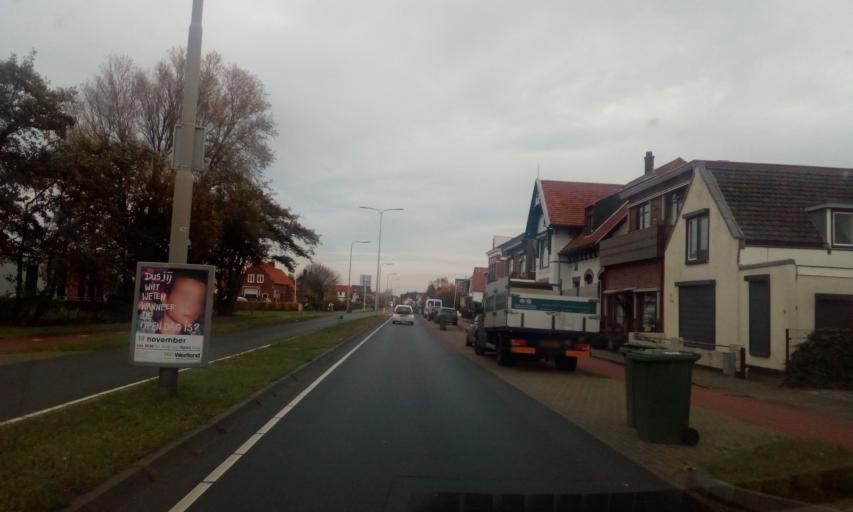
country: NL
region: South Holland
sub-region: Gemeente Westland
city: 's-Gravenzande
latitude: 52.0064
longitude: 4.1579
